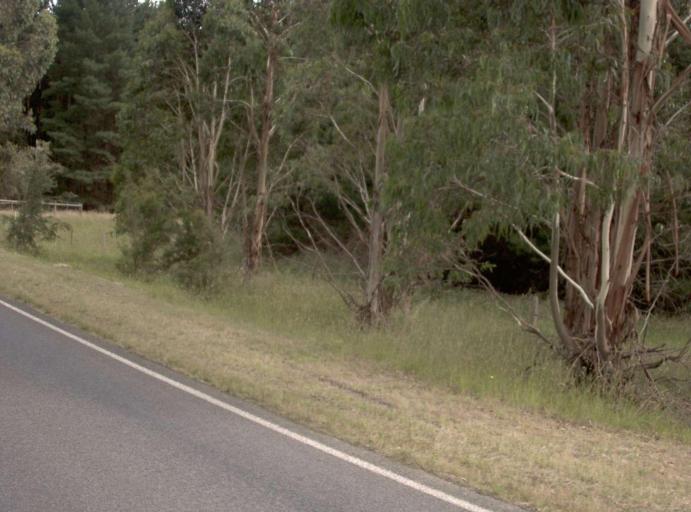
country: AU
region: Victoria
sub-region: Latrobe
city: Morwell
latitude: -38.1734
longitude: 146.4307
